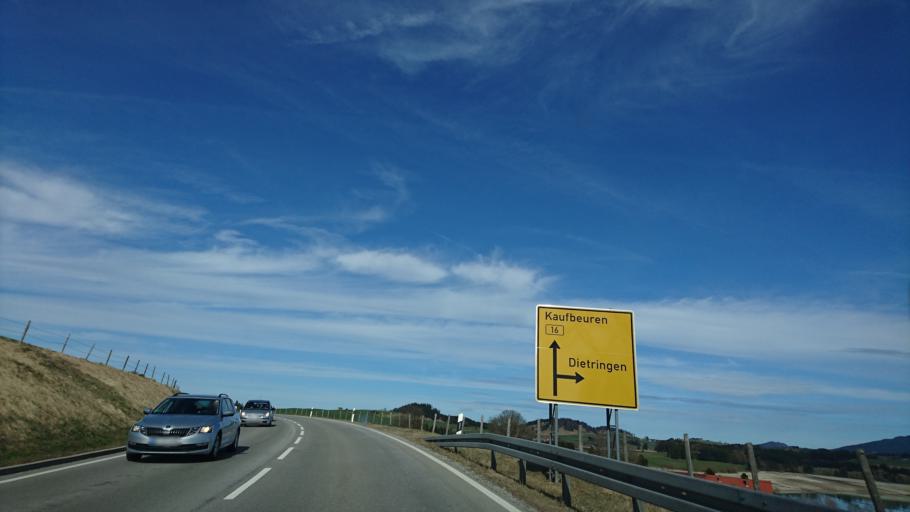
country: DE
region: Bavaria
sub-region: Swabia
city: Rosshaupten
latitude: 47.6341
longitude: 10.7327
